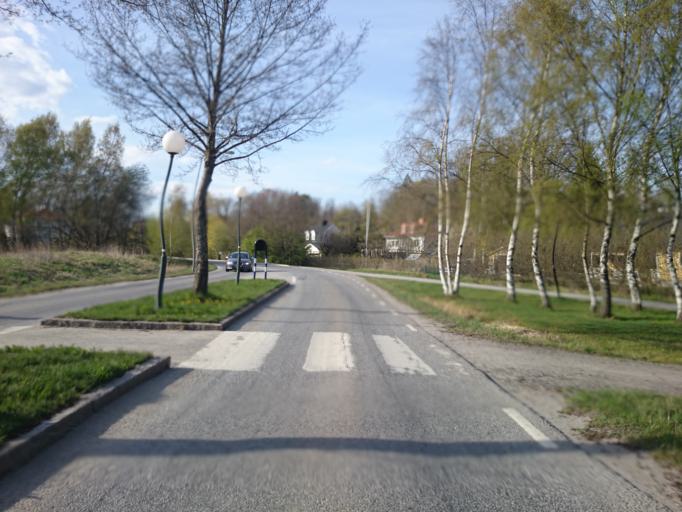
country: SE
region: Stockholm
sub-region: Huddinge Kommun
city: Huddinge
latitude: 59.2424
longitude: 17.9778
